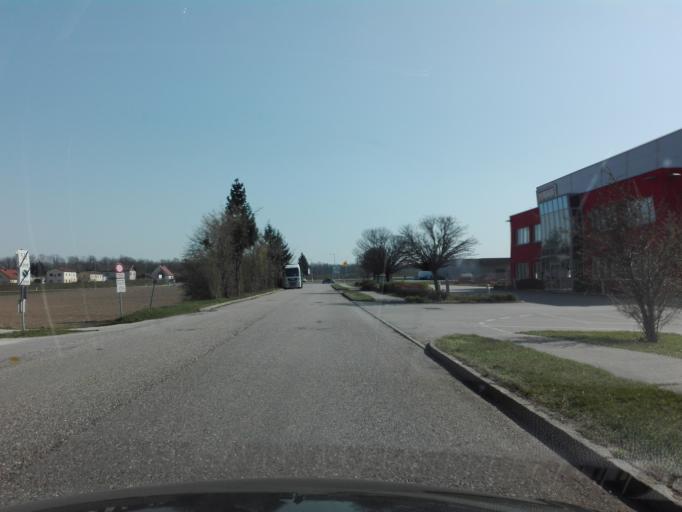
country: AT
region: Lower Austria
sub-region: Politischer Bezirk Amstetten
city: Ennsdorf
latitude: 48.2240
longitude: 14.5095
